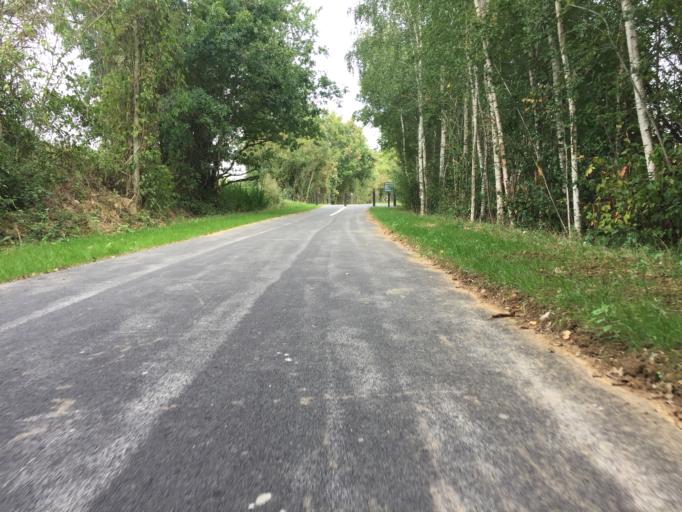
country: FR
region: Picardie
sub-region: Departement de l'Oise
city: Auneuil
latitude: 49.3813
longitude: 1.9931
